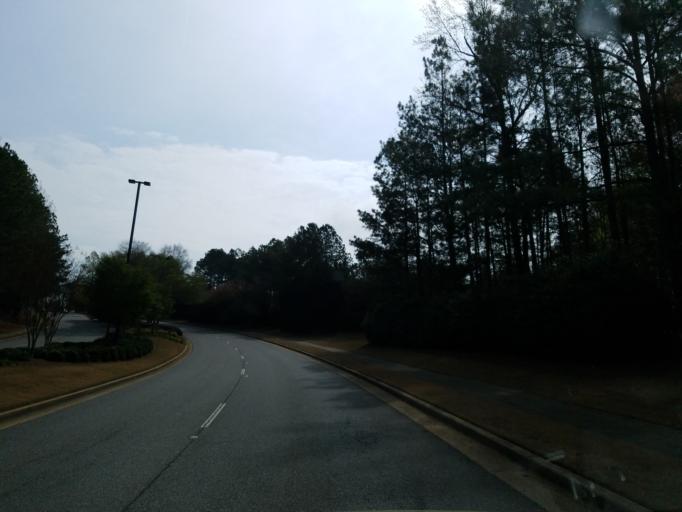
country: US
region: Georgia
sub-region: Fulton County
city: Alpharetta
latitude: 34.0891
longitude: -84.2315
